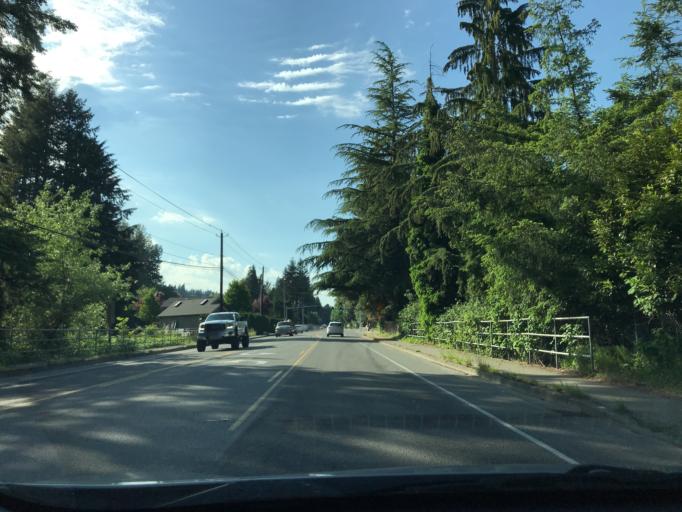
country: US
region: Washington
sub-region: King County
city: Issaquah
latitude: 47.5175
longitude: -122.0284
